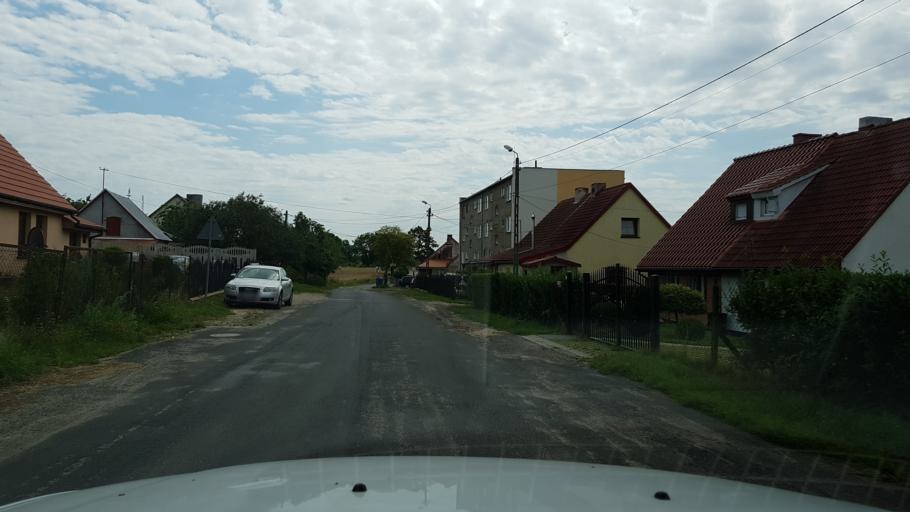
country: PL
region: West Pomeranian Voivodeship
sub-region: Powiat koszalinski
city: Mielno
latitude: 54.1699
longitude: 16.0545
